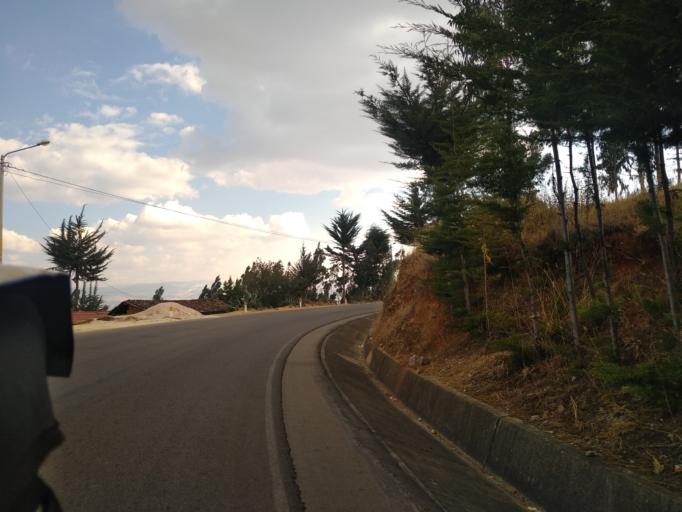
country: PE
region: Cajamarca
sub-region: Provincia de Cajamarca
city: Llacanora
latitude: -7.1460
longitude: -78.4094
